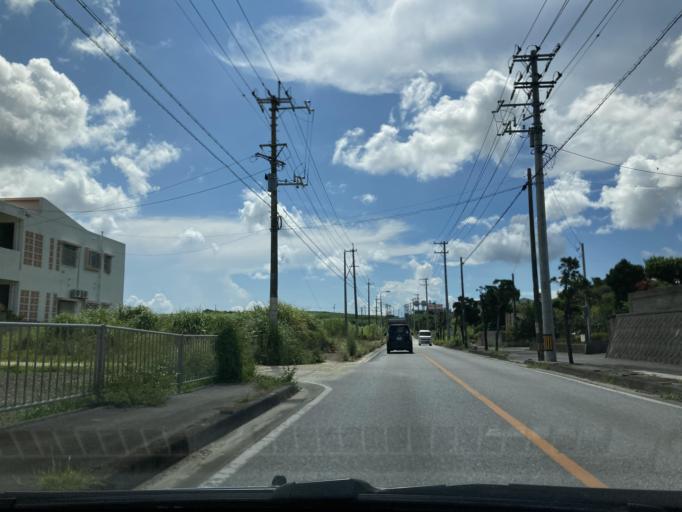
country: JP
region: Okinawa
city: Itoman
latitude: 26.1435
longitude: 127.7270
